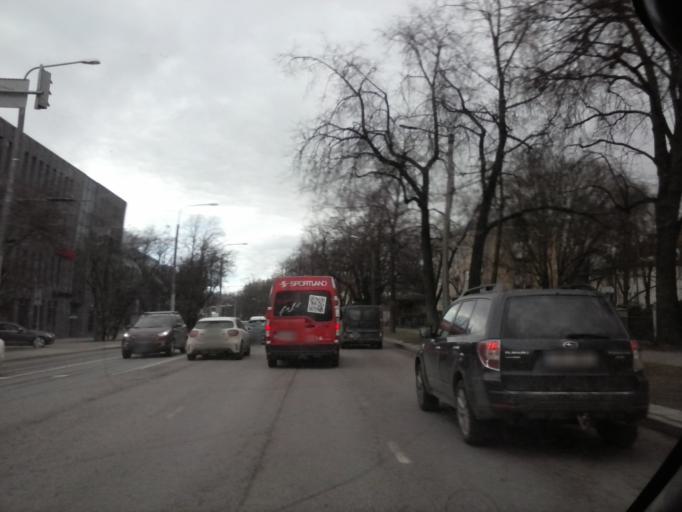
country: EE
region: Harju
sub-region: Tallinna linn
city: Tallinn
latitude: 59.4397
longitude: 24.7805
